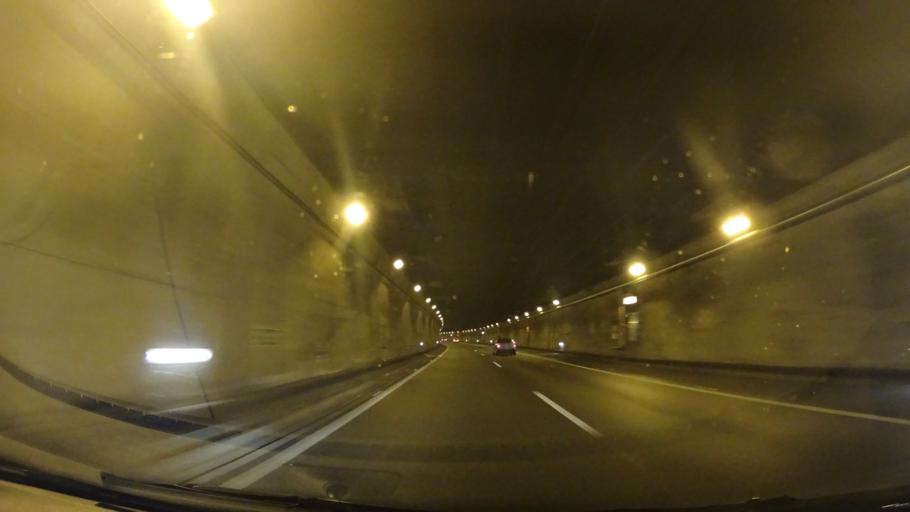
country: ES
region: Madrid
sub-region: Provincia de Madrid
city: Guadarrama
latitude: 40.7167
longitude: -4.1558
